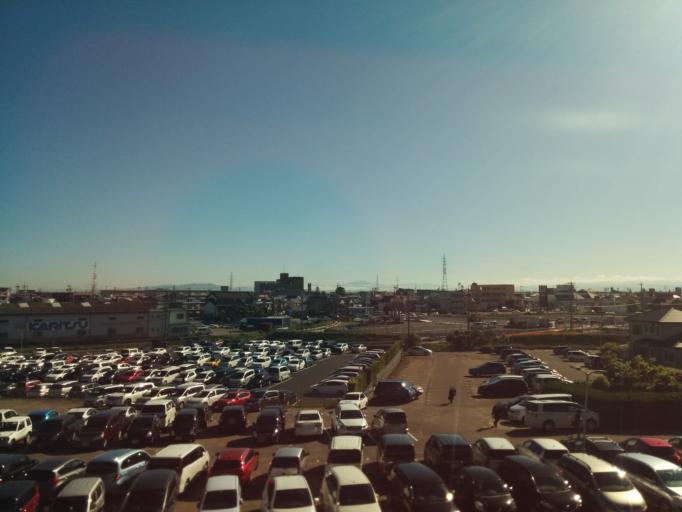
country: JP
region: Aichi
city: Chiryu
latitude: 35.0043
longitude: 137.0167
